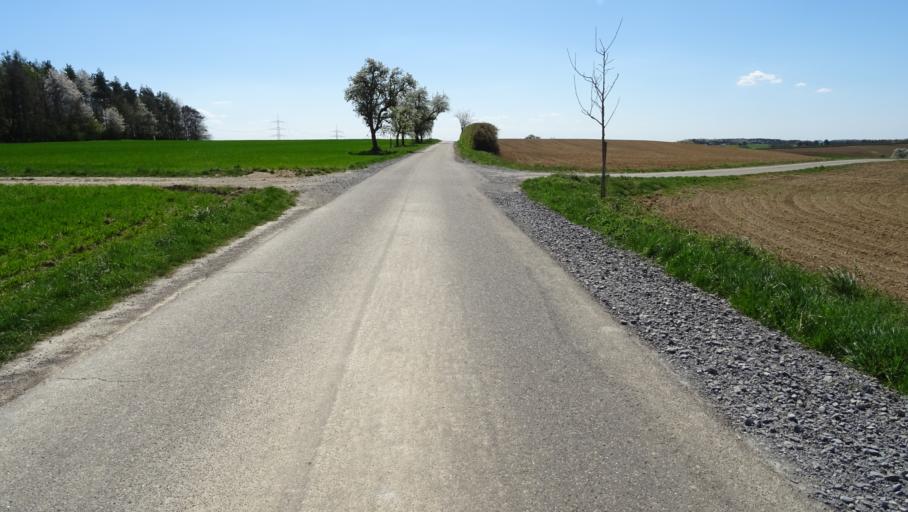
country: DE
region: Baden-Wuerttemberg
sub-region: Karlsruhe Region
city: Billigheim
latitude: 49.3992
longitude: 9.2452
